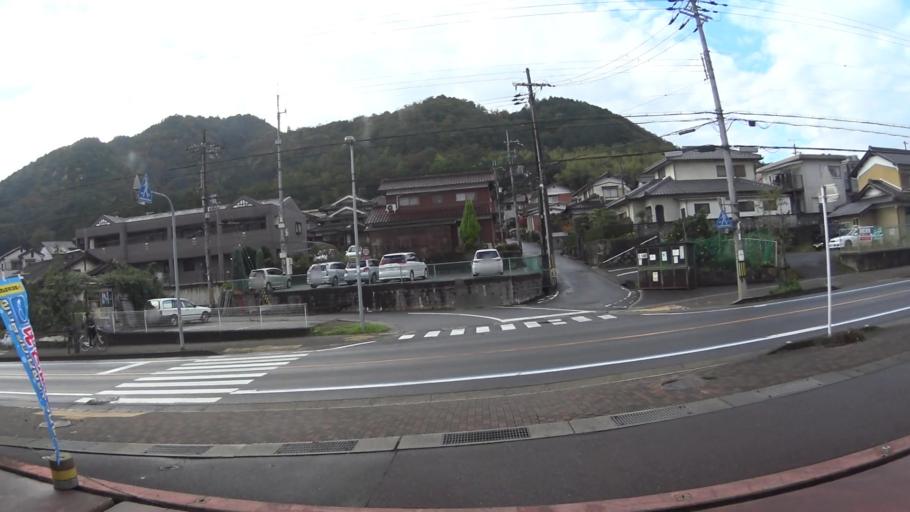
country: JP
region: Kyoto
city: Ayabe
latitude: 35.3057
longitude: 135.2202
